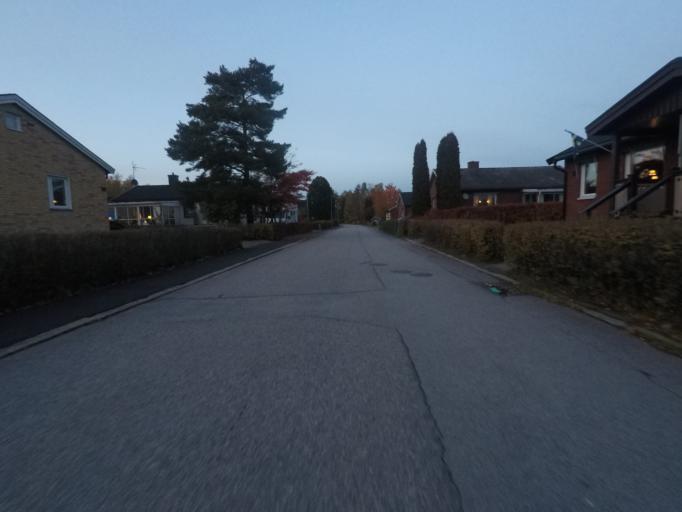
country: SE
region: OErebro
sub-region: Karlskoga Kommun
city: Karlskoga
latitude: 59.3054
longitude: 14.5006
